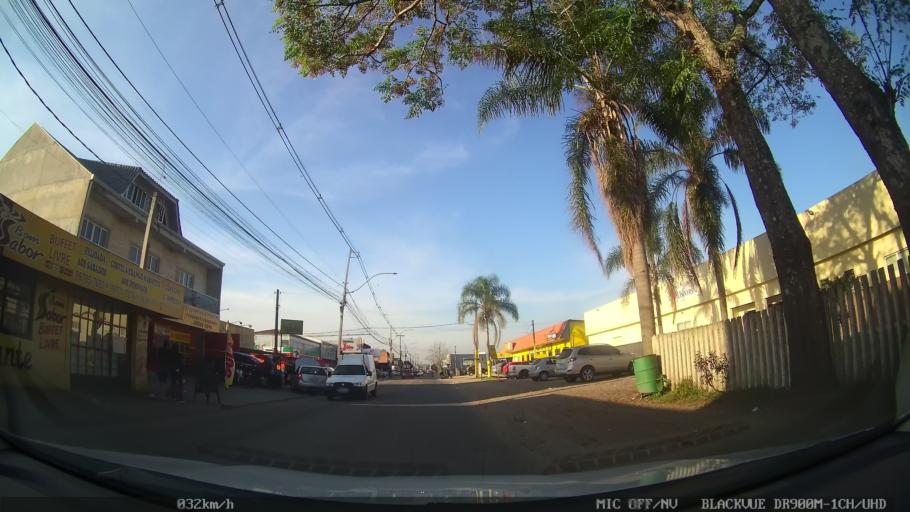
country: BR
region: Parana
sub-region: Pinhais
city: Pinhais
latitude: -25.4553
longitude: -49.1534
